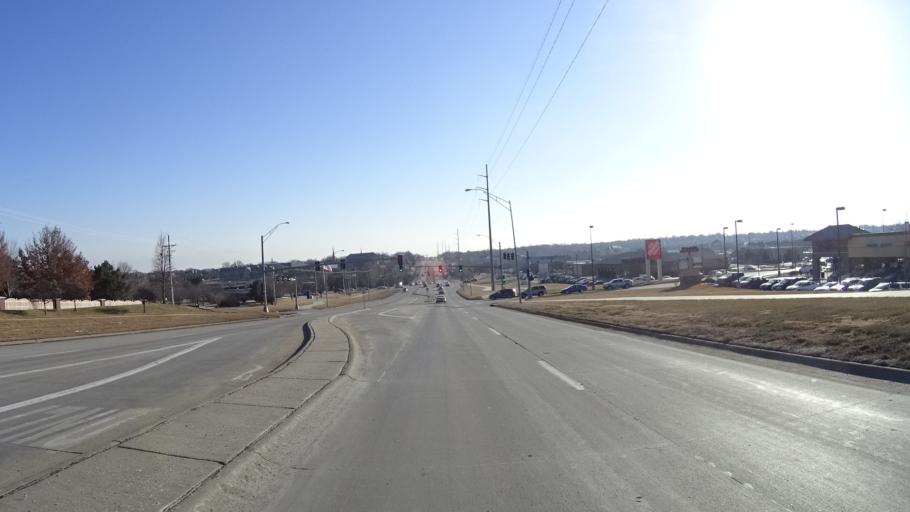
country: US
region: Nebraska
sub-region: Douglas County
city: Bennington
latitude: 41.2950
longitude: -96.1390
